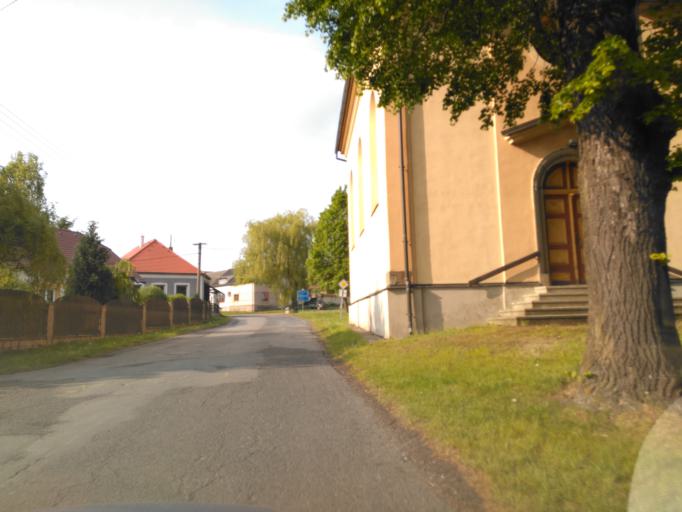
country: CZ
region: Plzensky
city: Zbiroh
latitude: 49.8843
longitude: 13.8046
